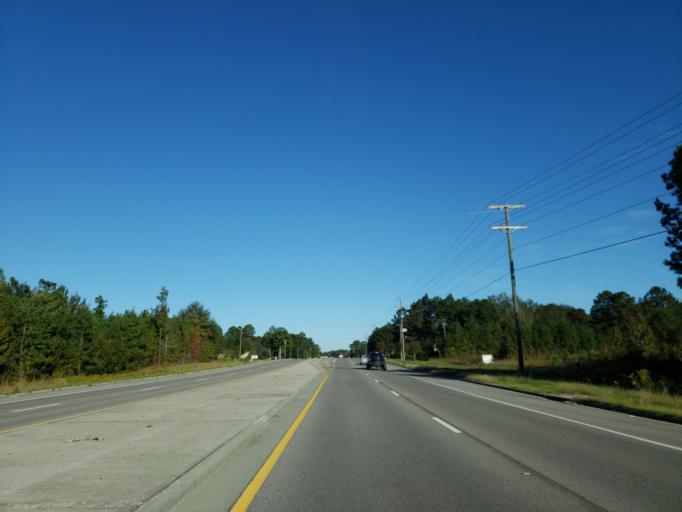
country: US
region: Mississippi
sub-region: Forrest County
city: Petal
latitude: 31.3506
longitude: -89.1913
